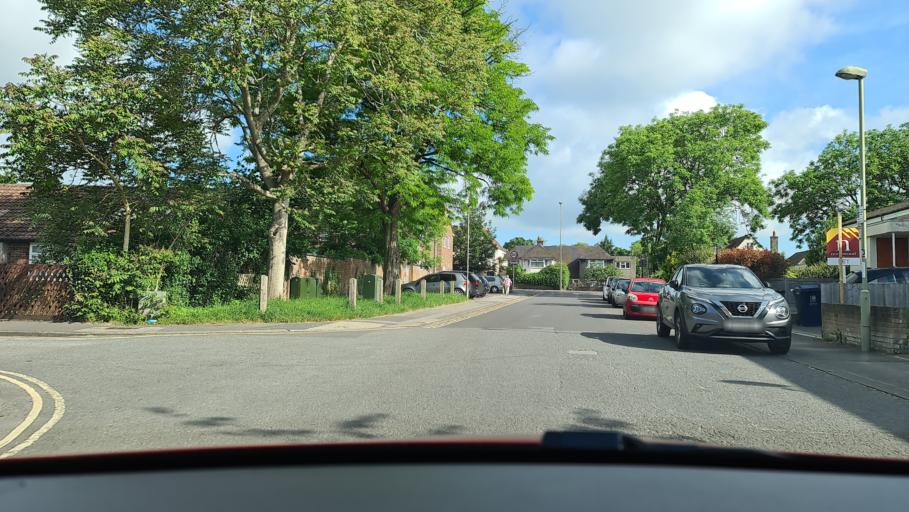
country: GB
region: England
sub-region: Oxfordshire
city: Cowley
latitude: 51.7615
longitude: -1.2019
